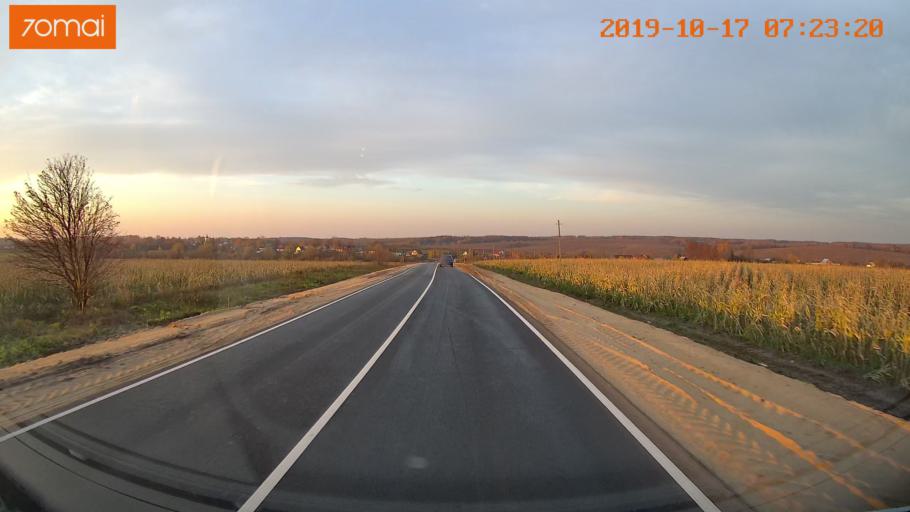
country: RU
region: Ivanovo
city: Gavrilov Posad
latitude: 56.3355
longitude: 40.1221
